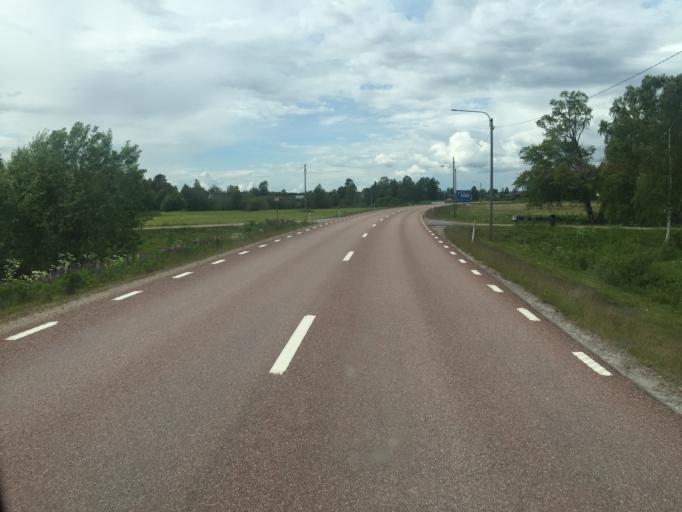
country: SE
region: Dalarna
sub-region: Vansbro Kommun
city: Vansbro
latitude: 60.4742
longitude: 14.0904
